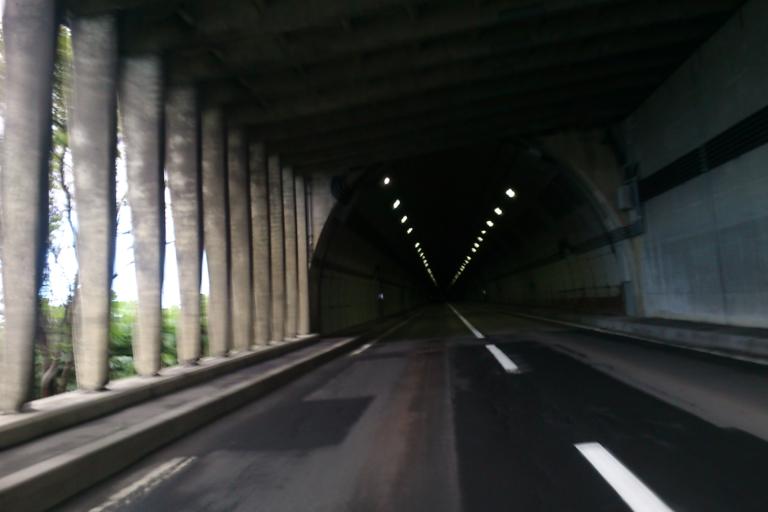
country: JP
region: Hokkaido
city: Ishikari
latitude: 43.4380
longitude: 141.4164
